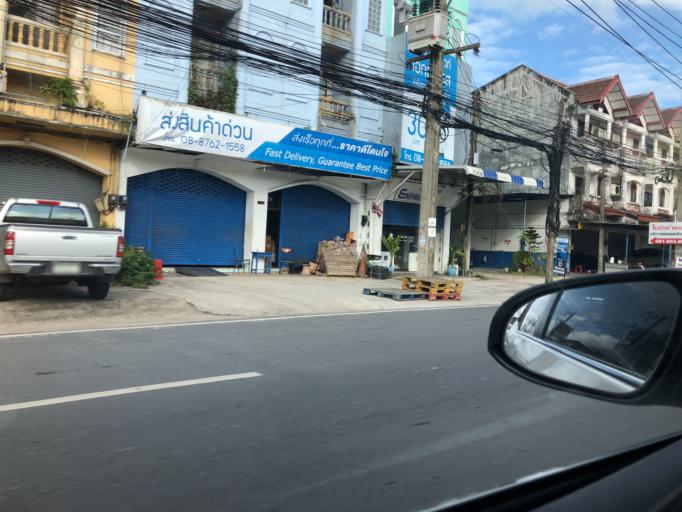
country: TH
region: Phuket
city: Ban Ko Kaeo
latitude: 7.9411
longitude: 98.3946
